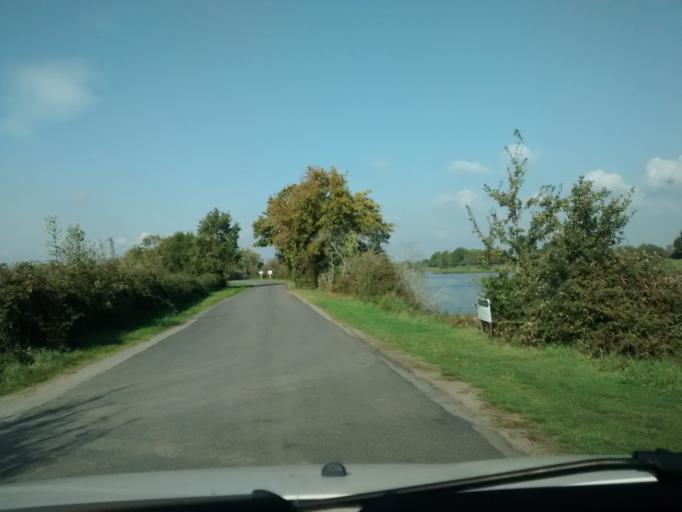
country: FR
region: Pays de la Loire
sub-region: Departement de la Loire-Atlantique
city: Frossay
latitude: 47.2492
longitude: -1.8969
